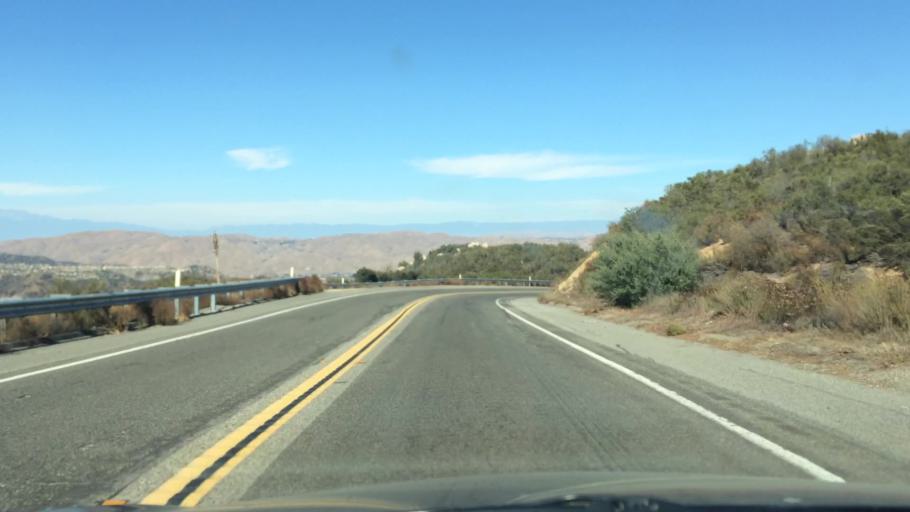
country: US
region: California
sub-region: Riverside County
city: Lakeland Village
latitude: 33.6542
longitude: -117.4026
